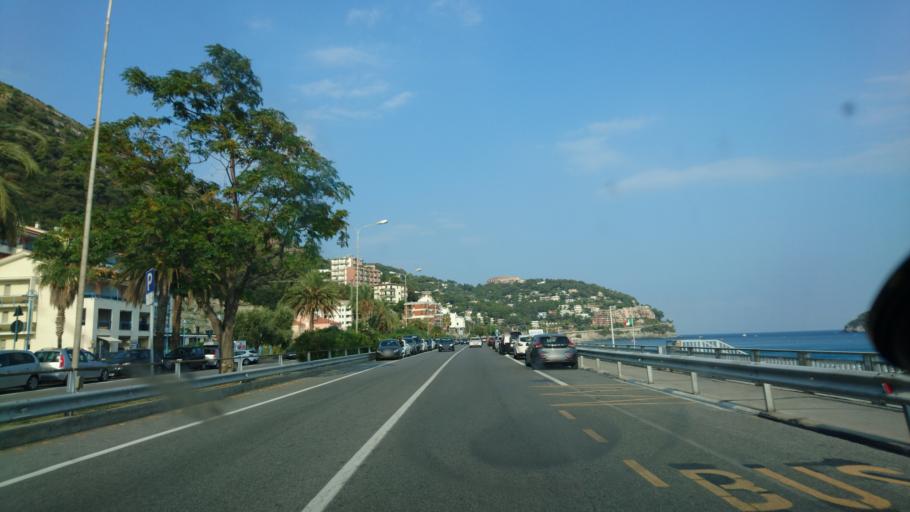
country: IT
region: Liguria
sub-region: Provincia di Savona
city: Spotorno
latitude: 44.2341
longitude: 8.4290
